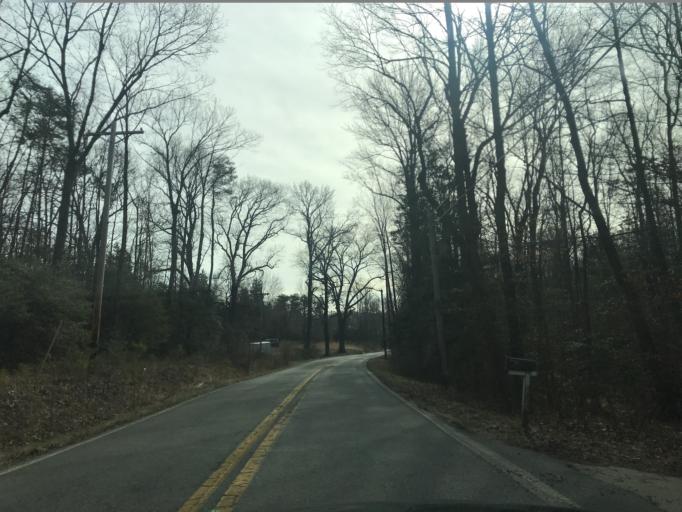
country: US
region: Virginia
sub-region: King George County
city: Dahlgren
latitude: 38.4154
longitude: -77.1681
